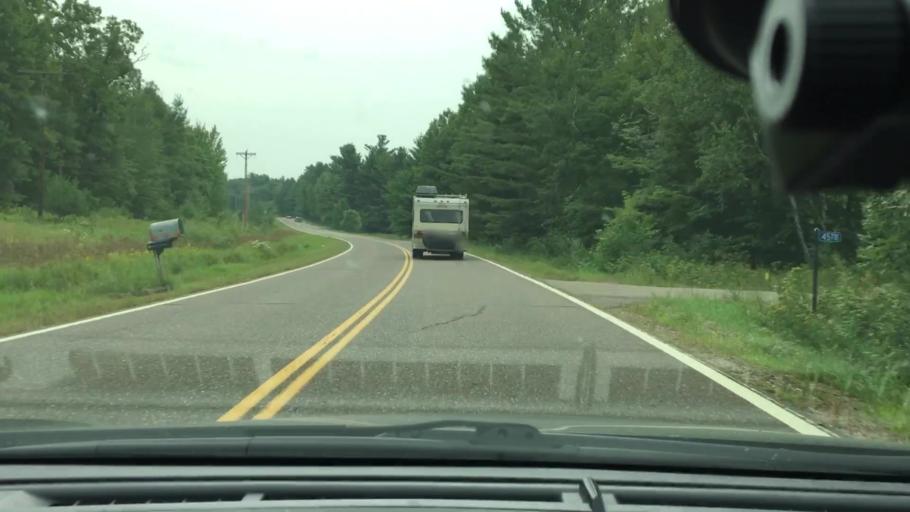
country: US
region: Minnesota
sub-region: Aitkin County
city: Aitkin
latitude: 46.4045
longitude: -93.8063
